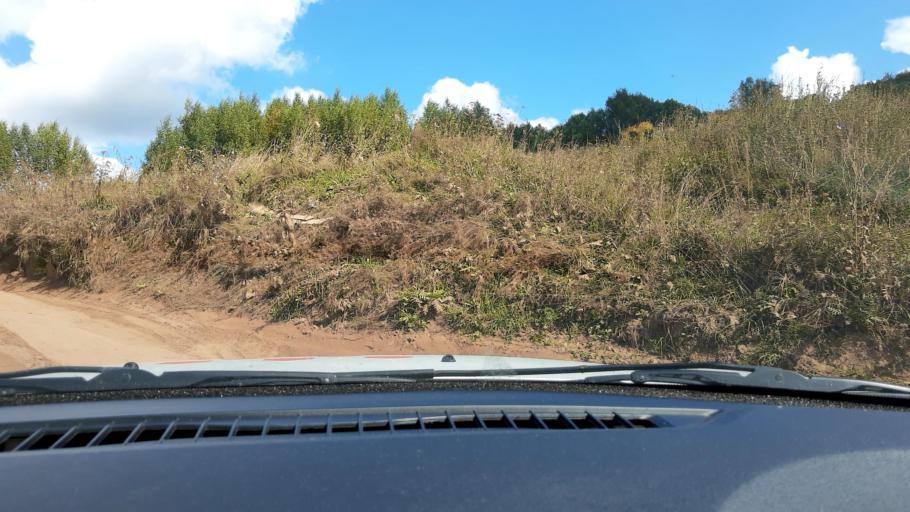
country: RU
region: Nizjnij Novgorod
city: Nizhniy Novgorod
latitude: 56.1990
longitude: 43.9634
